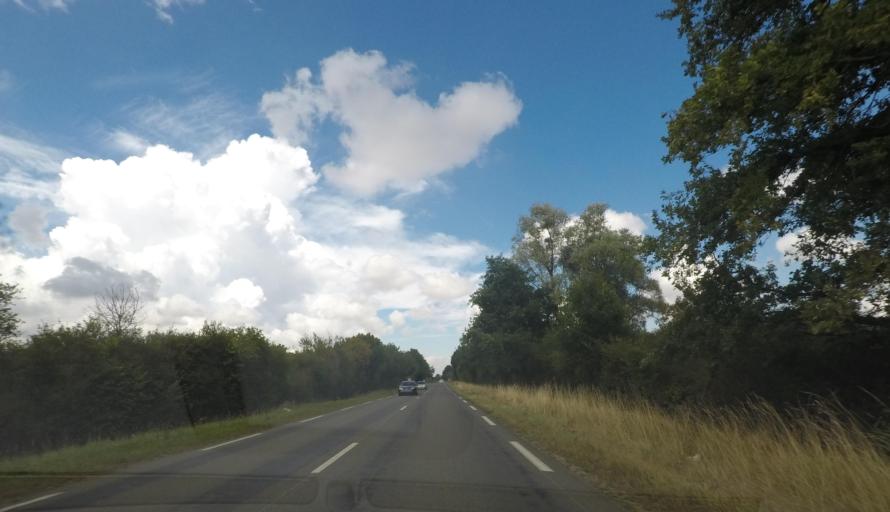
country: FR
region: Pays de la Loire
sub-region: Departement de la Sarthe
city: Bonnetable
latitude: 48.2178
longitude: 0.4314
